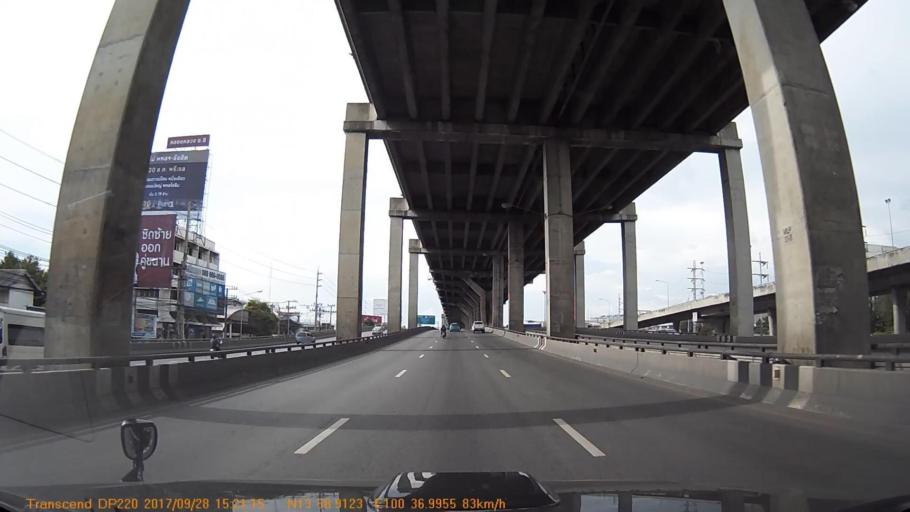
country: TH
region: Bangkok
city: Sai Mai
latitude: 13.9821
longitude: 100.6166
